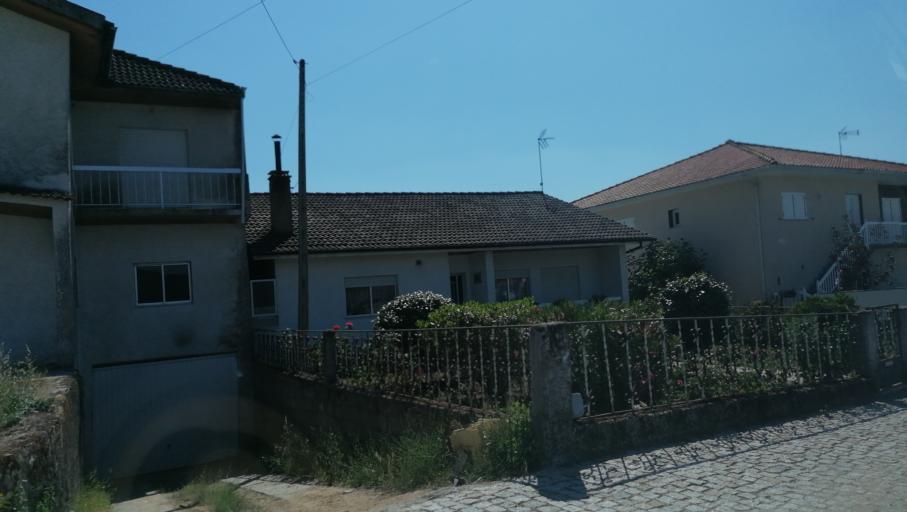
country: PT
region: Viseu
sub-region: Tarouca
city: Tarouca
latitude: 41.0184
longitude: -7.7105
